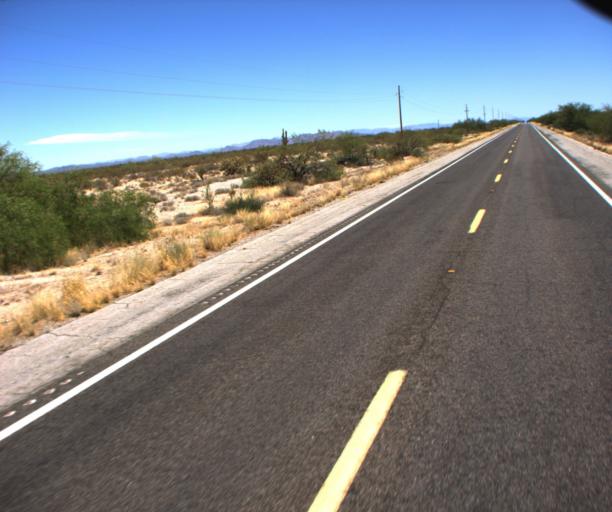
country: US
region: Arizona
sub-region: La Paz County
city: Salome
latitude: 33.8895
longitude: -113.3376
